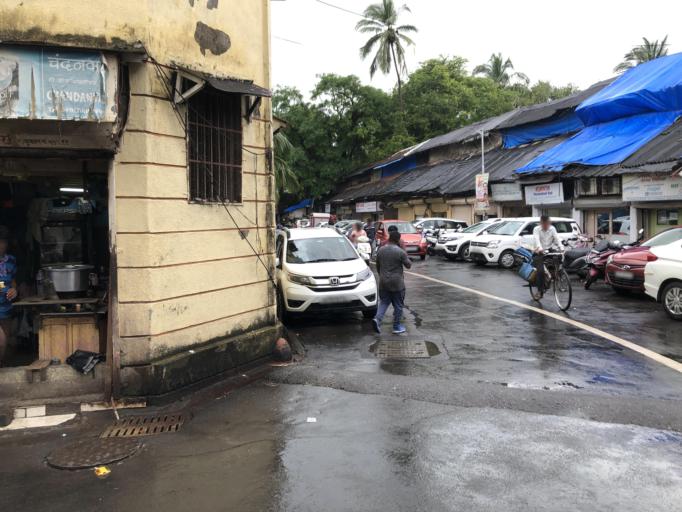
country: IN
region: Maharashtra
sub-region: Raigarh
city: Uran
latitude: 18.9459
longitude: 72.8251
